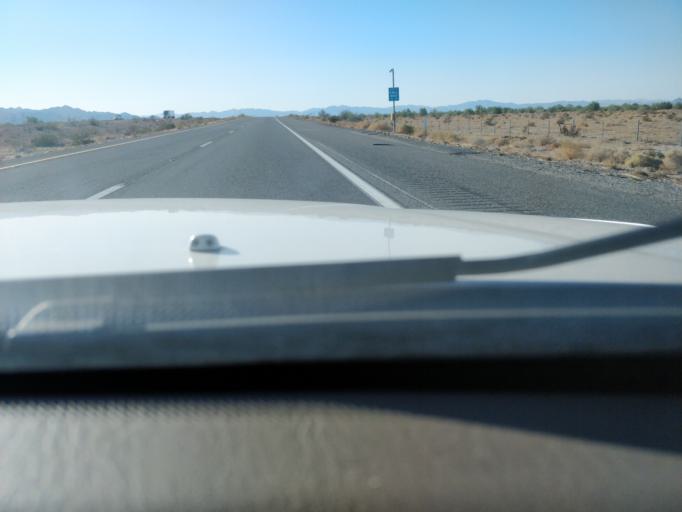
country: US
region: California
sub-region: Riverside County
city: Mesa Verde
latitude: 33.6700
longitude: -115.2003
